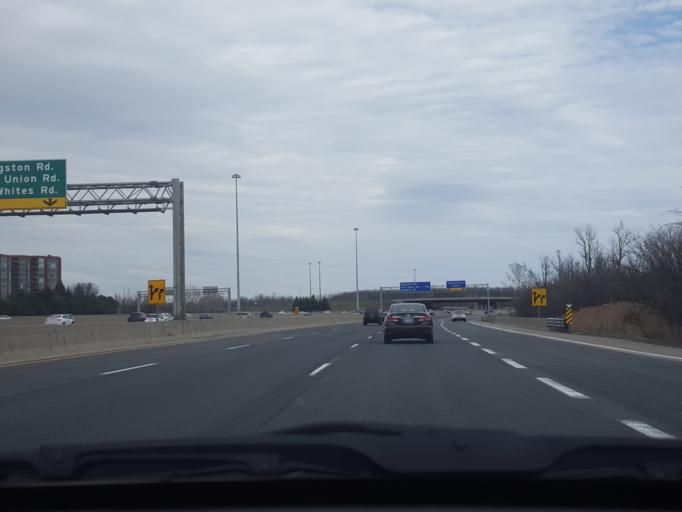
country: CA
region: Ontario
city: Scarborough
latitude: 43.7994
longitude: -79.1746
